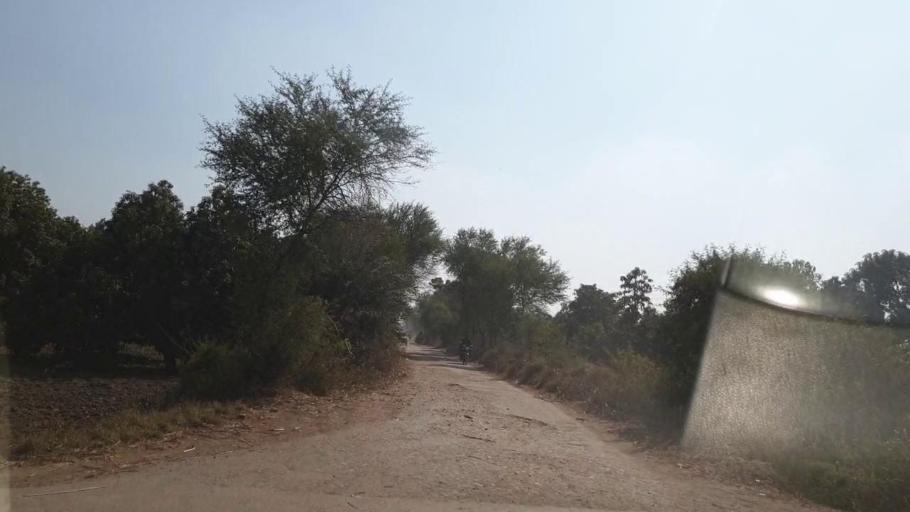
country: PK
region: Sindh
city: Matiari
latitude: 25.5064
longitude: 68.4653
